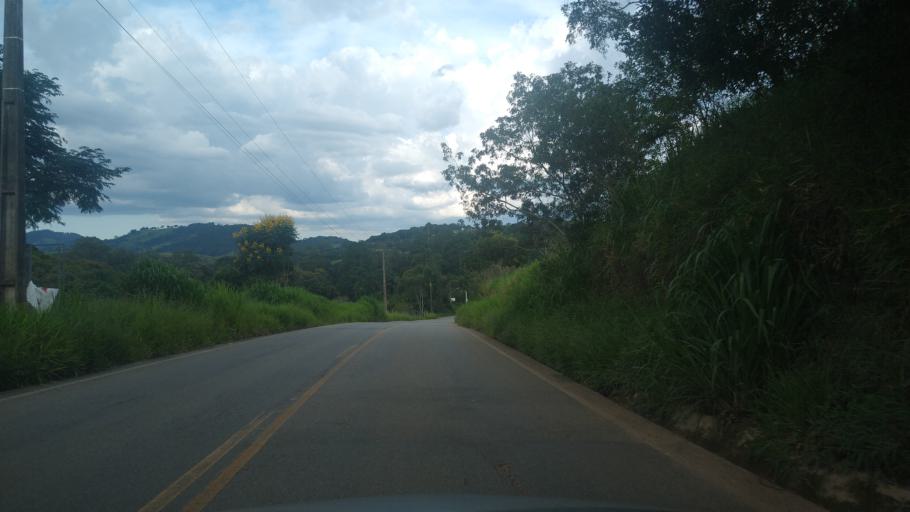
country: BR
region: Minas Gerais
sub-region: Extrema
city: Extrema
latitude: -22.8068
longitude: -46.3057
